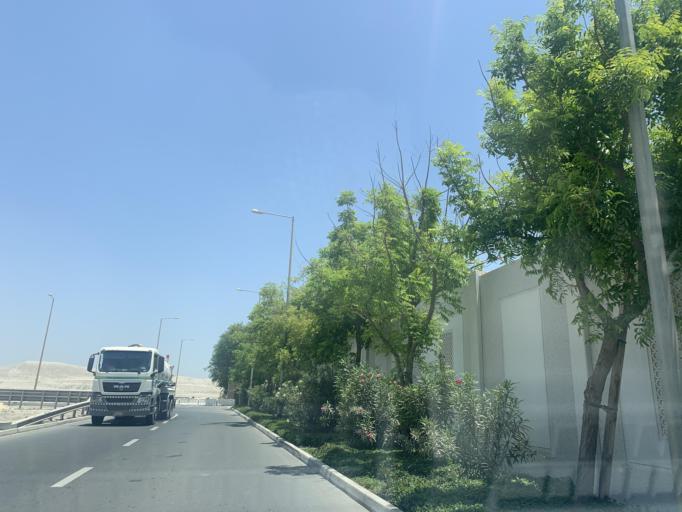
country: BH
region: Manama
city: Jidd Hafs
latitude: 26.2387
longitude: 50.4717
